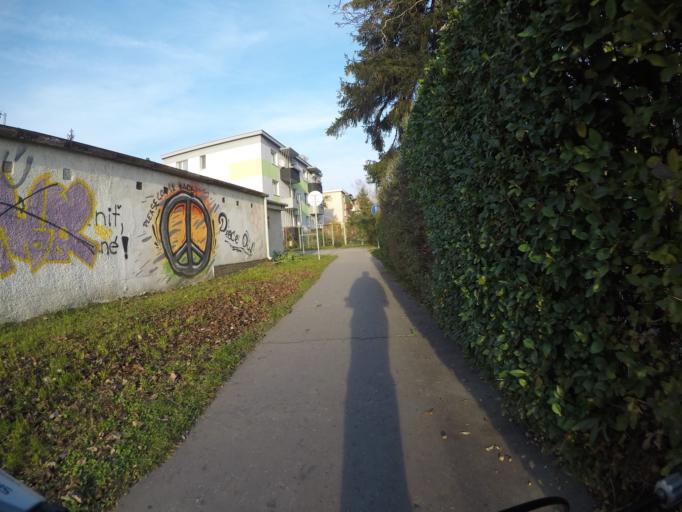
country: SK
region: Bratislavsky
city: Bratislava
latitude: 48.1733
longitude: 17.1583
